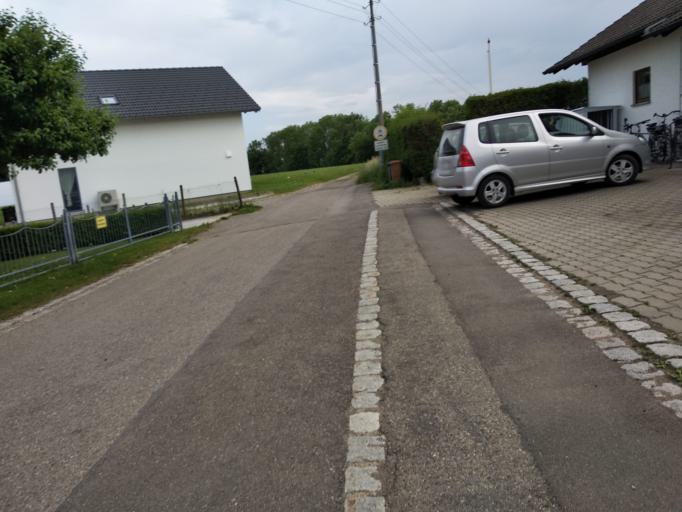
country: DE
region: Bavaria
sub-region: Swabia
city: Lachen
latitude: 47.9439
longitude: 10.2208
